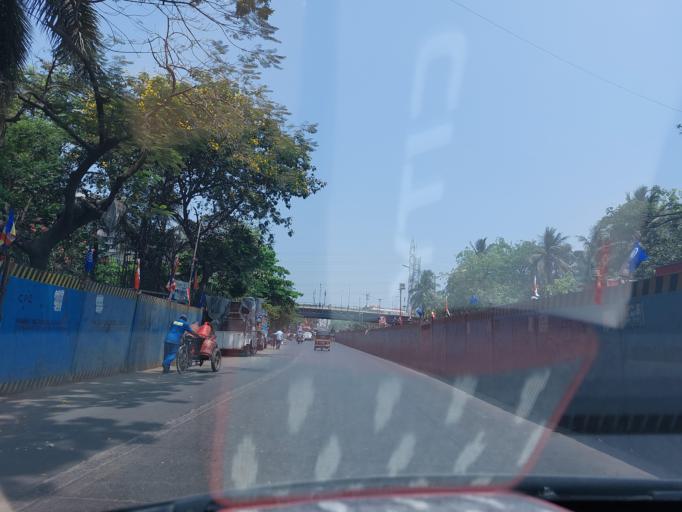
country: IN
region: Maharashtra
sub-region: Mumbai Suburban
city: Mumbai
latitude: 19.0555
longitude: 72.8882
